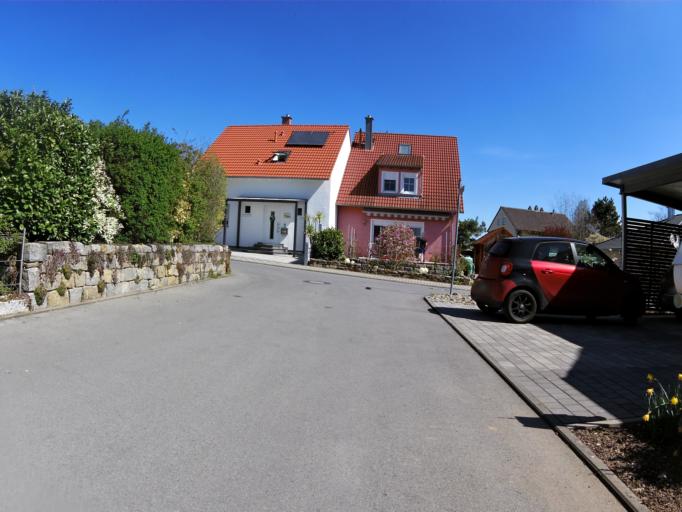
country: DE
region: Bavaria
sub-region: Regierungsbezirk Unterfranken
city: Volkach
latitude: 49.8612
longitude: 10.2107
